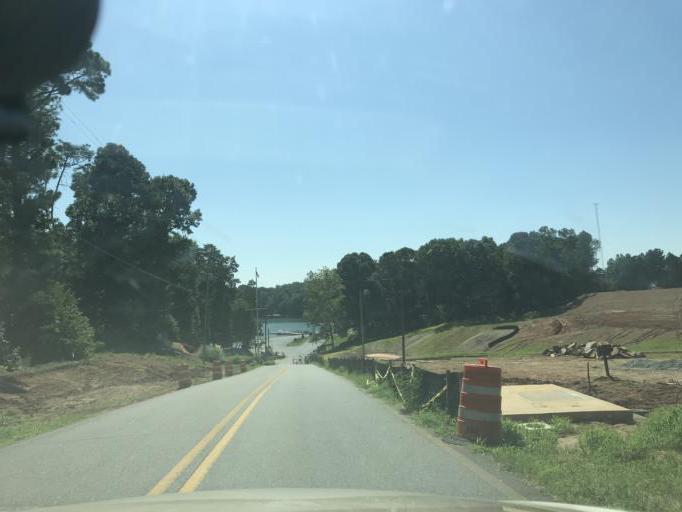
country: US
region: Georgia
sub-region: Forsyth County
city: Cumming
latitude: 34.2108
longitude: -84.1026
